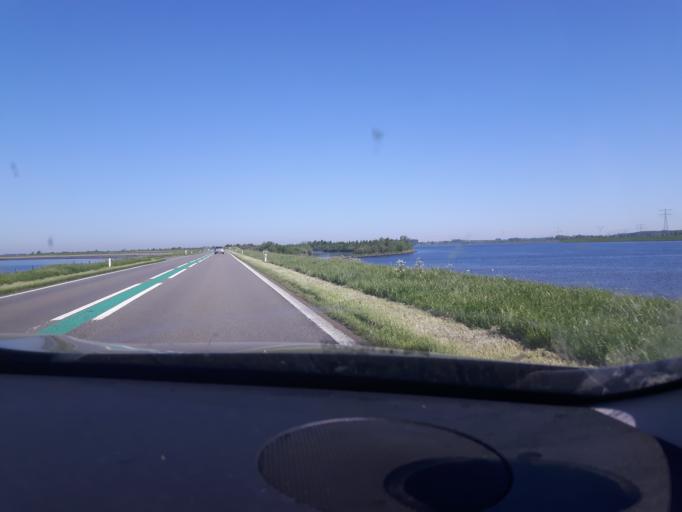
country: NL
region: Zeeland
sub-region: Gemeente Tholen
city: Tholen
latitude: 51.4846
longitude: 4.2188
